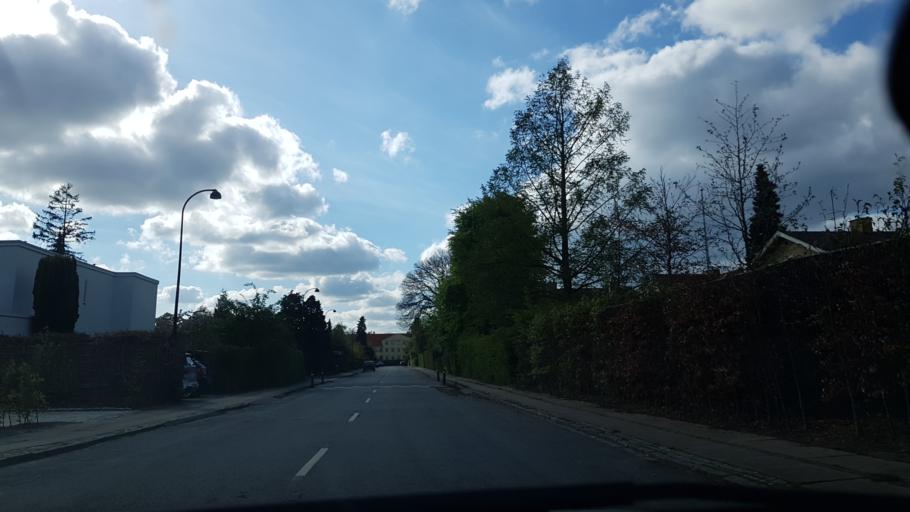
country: DK
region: Capital Region
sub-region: Gentofte Kommune
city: Charlottenlund
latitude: 55.7661
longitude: 12.5913
